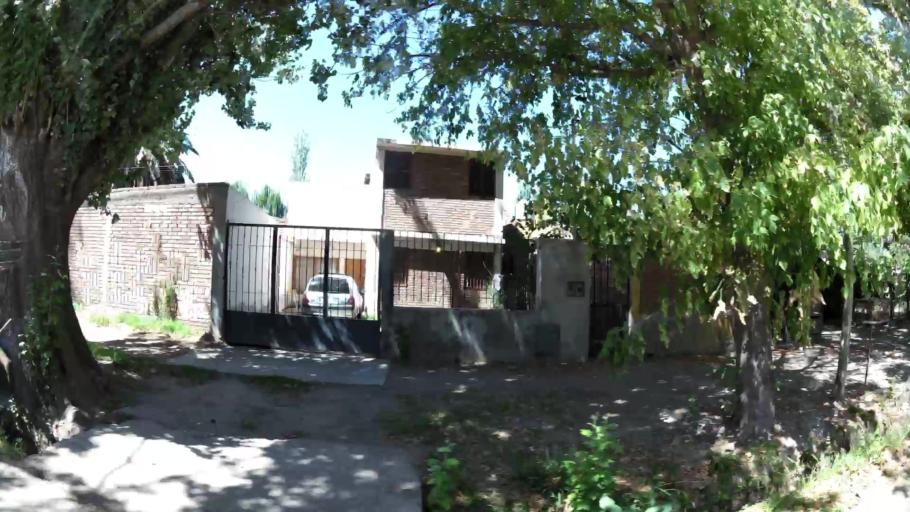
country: AR
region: Mendoza
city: Las Heras
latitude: -32.8685
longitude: -68.8002
